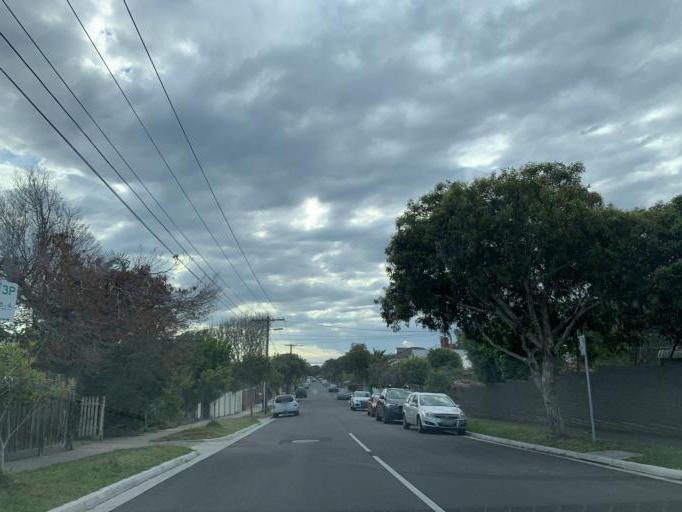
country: AU
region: Victoria
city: Hampton
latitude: -37.9533
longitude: 145.0087
